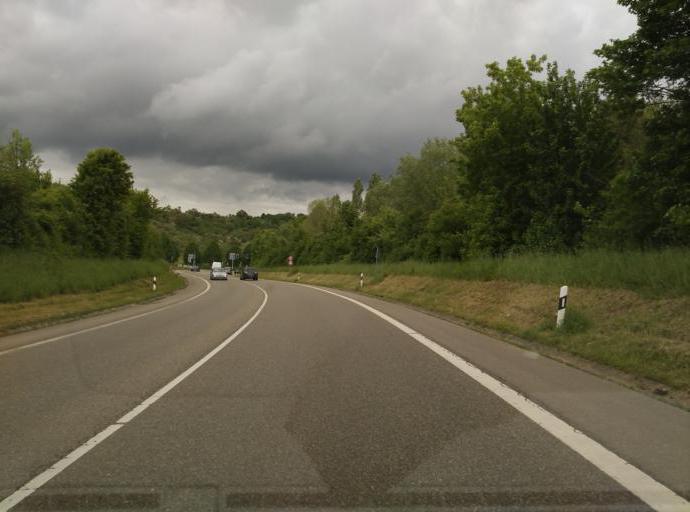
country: DE
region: Baden-Wuerttemberg
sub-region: Regierungsbezirk Stuttgart
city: Neckartailfingen
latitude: 48.6150
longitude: 9.2778
